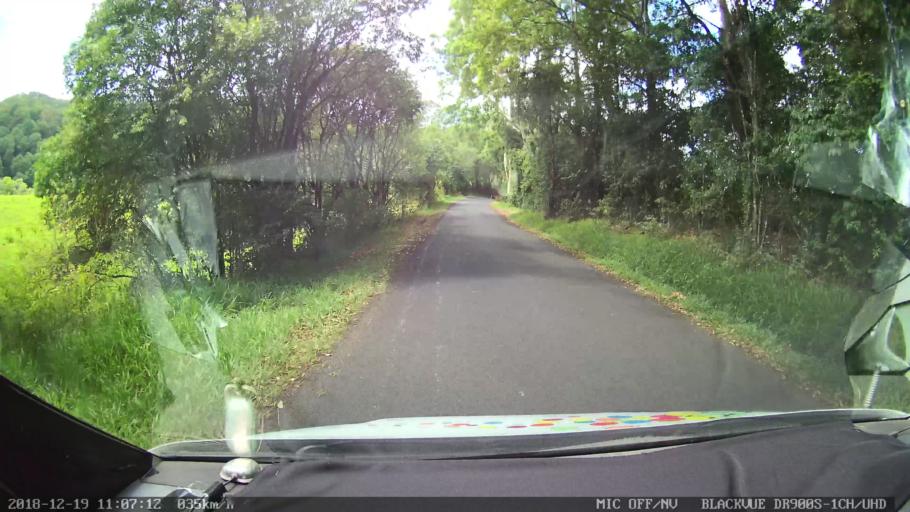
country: AU
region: New South Wales
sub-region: Lismore Municipality
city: Nimbin
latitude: -28.6251
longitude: 153.2665
